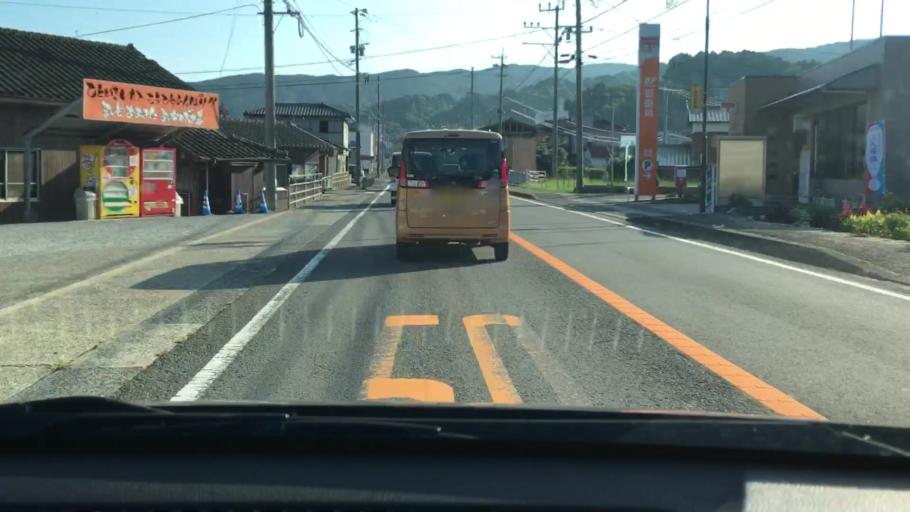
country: JP
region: Nagasaki
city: Togitsu
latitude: 32.9085
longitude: 129.7830
